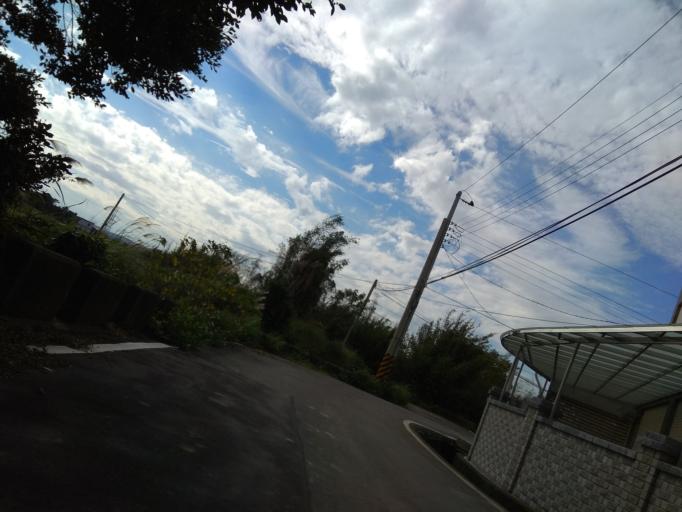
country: TW
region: Taiwan
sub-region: Hsinchu
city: Zhubei
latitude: 24.9537
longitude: 121.1056
